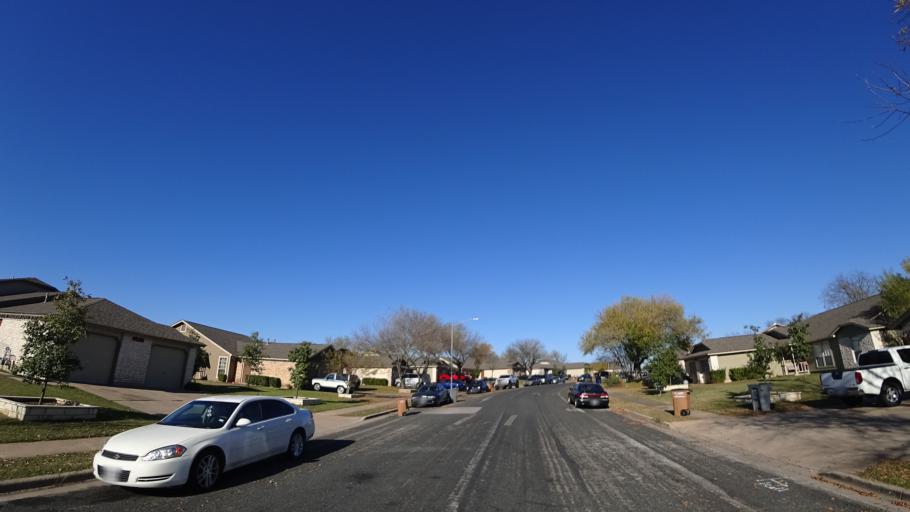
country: US
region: Texas
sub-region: Travis County
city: Wells Branch
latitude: 30.4072
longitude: -97.6944
